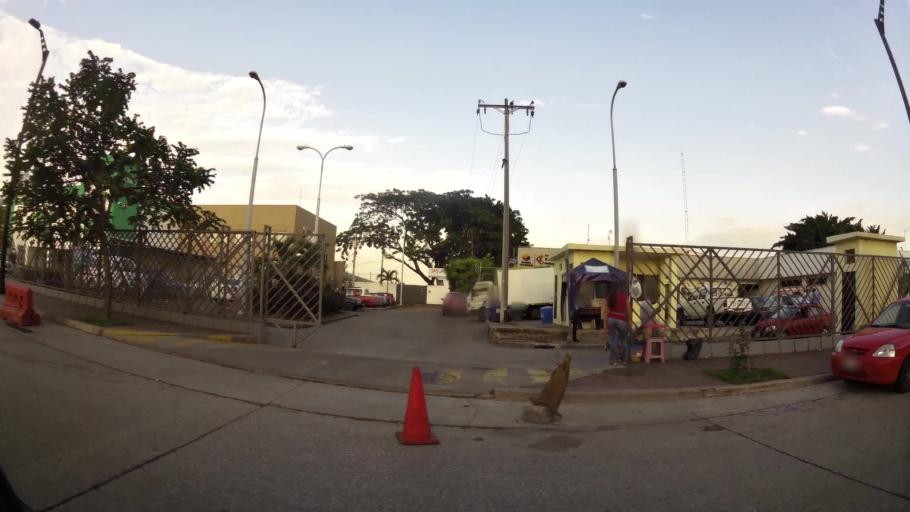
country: EC
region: Guayas
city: Eloy Alfaro
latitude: -2.1600
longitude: -79.8892
